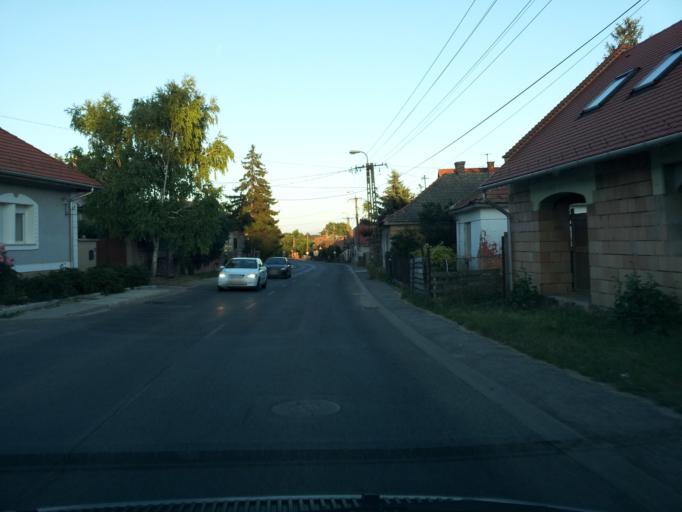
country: HU
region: Veszprem
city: Szentkiralyszabadja
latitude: 47.0142
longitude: 17.9548
